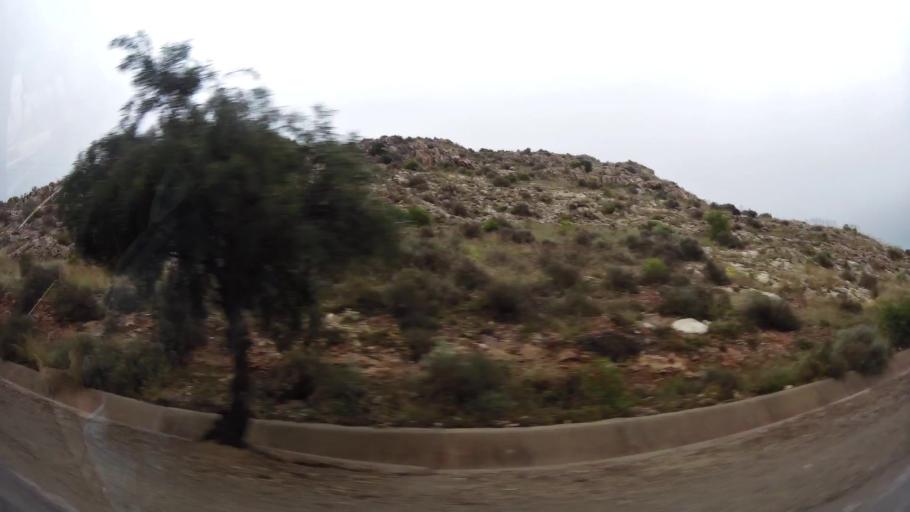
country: MA
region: Taza-Al Hoceima-Taounate
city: Al Hoceima
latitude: 35.2174
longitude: -3.9210
